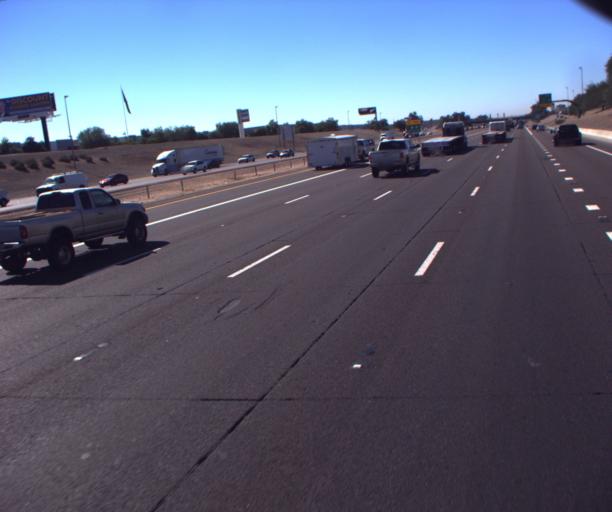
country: US
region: Arizona
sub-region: Maricopa County
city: Tolleson
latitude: 33.4629
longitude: -112.2124
